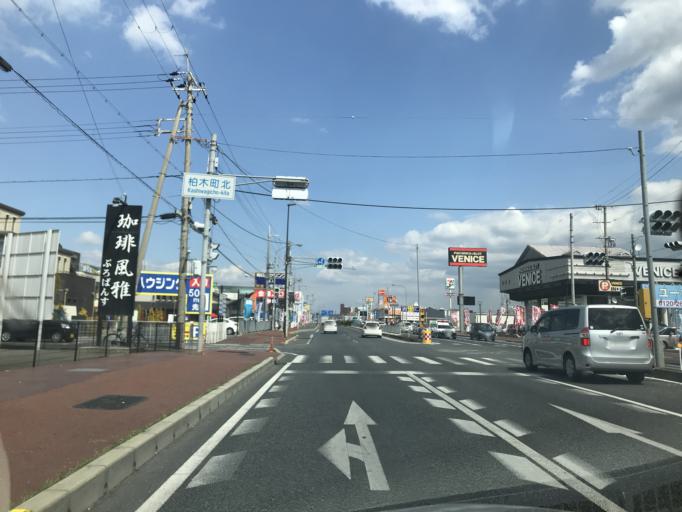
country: JP
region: Nara
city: Nara-shi
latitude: 34.6746
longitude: 135.8004
